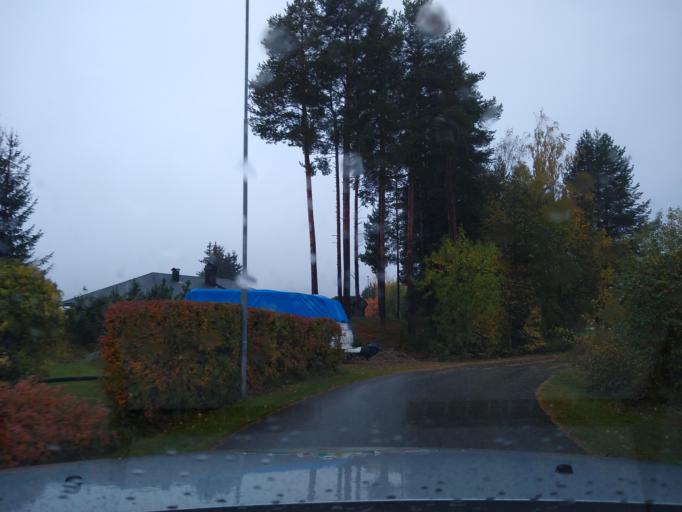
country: NO
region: Oppland
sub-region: Ringebu
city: Ringebu
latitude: 61.5386
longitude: 10.1371
